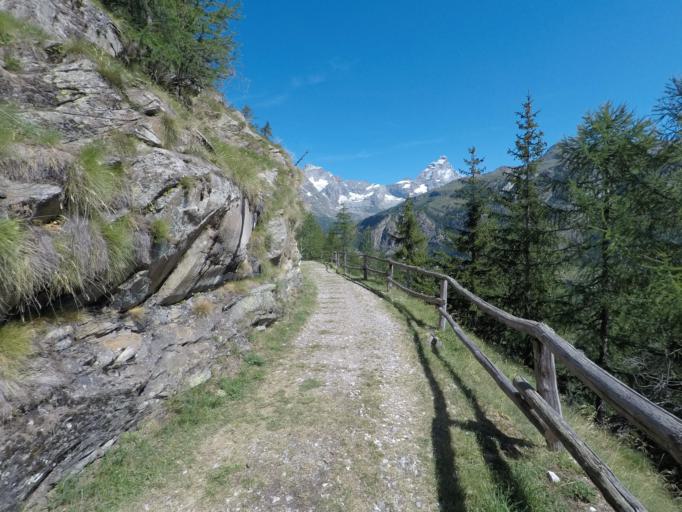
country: IT
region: Aosta Valley
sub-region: Valle d'Aosta
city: Valtournenche
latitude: 45.8786
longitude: 7.6185
